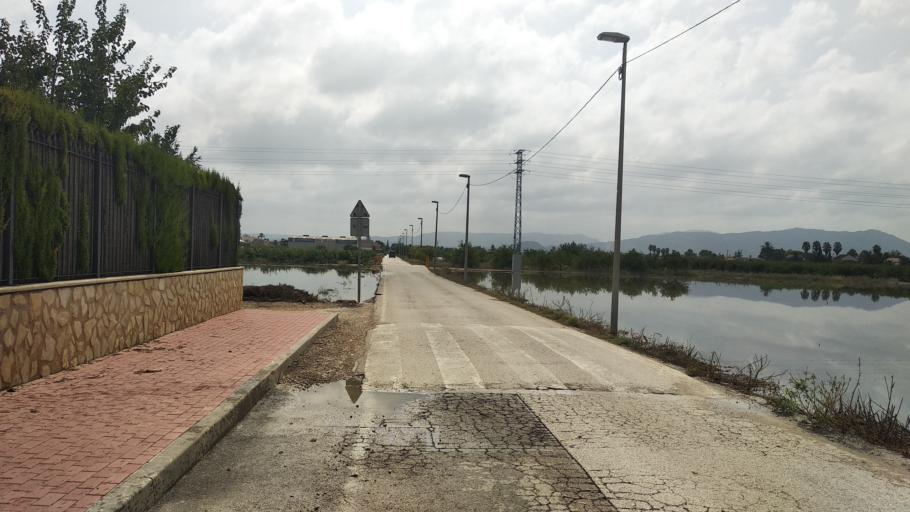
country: ES
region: Murcia
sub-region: Murcia
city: Santomera
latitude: 38.0450
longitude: -1.0370
